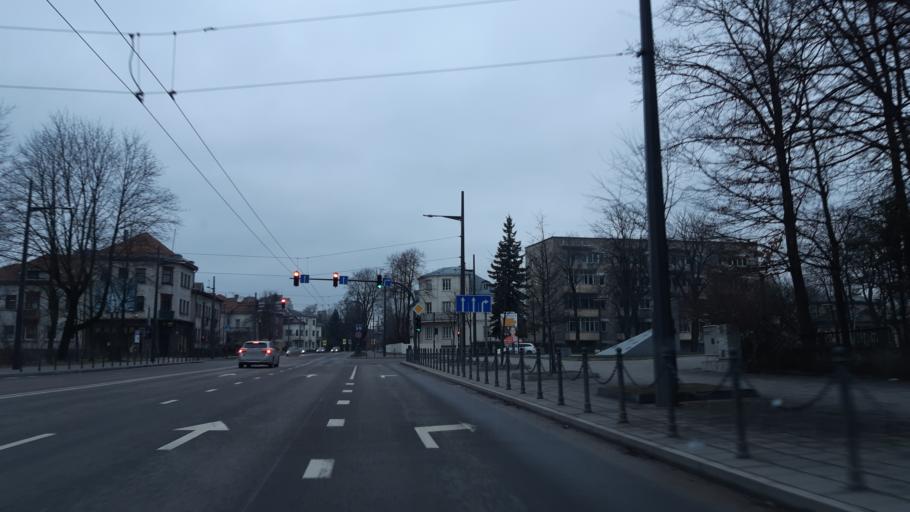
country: LT
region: Kauno apskritis
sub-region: Kaunas
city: Eiguliai
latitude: 54.9000
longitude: 23.9320
